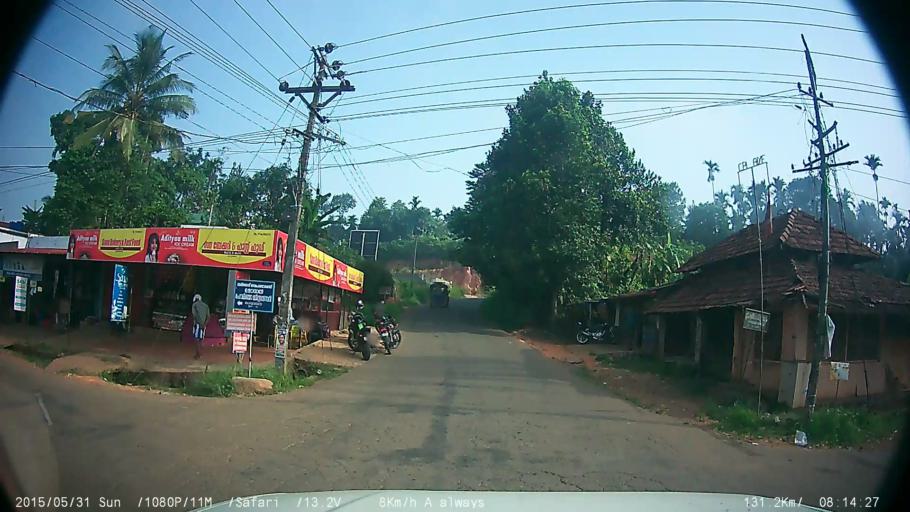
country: IN
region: Kerala
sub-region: Wayanad
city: Kalpetta
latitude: 11.6436
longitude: 76.0032
